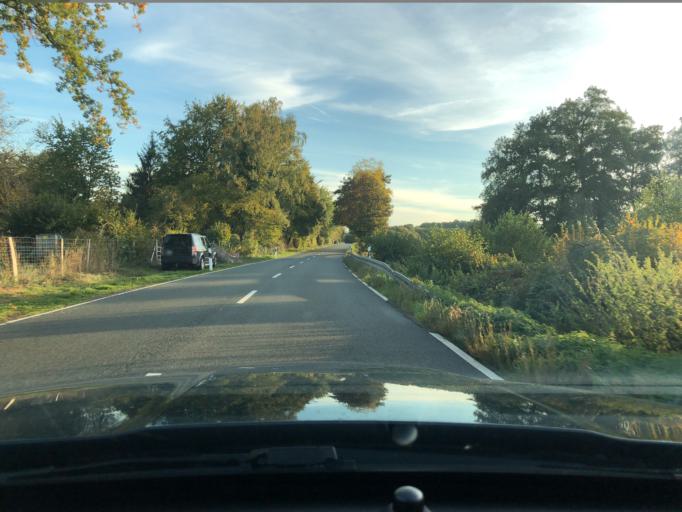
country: DE
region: North Rhine-Westphalia
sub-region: Regierungsbezirk Munster
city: Telgte
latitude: 51.9936
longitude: 7.7148
